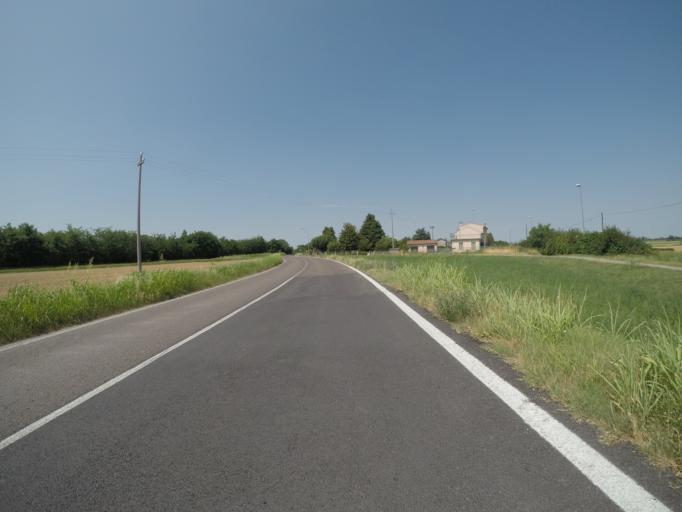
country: IT
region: Veneto
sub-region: Provincia di Rovigo
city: Pincara
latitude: 45.0038
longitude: 11.6359
